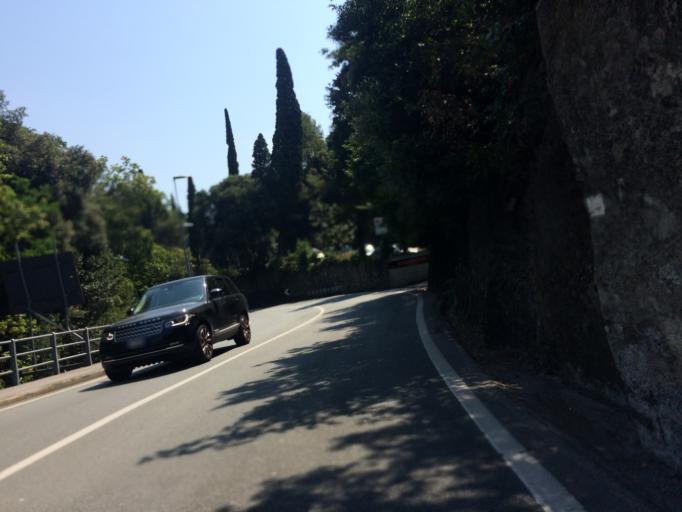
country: IT
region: Liguria
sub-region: Provincia di Genova
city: Arenzano
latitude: 44.4006
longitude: 8.6808
